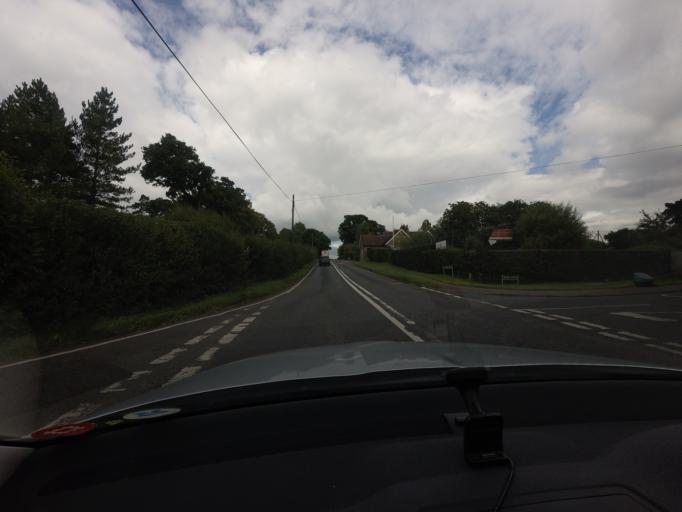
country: GB
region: England
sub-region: Kent
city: Tonbridge
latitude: 51.2440
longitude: 0.2788
